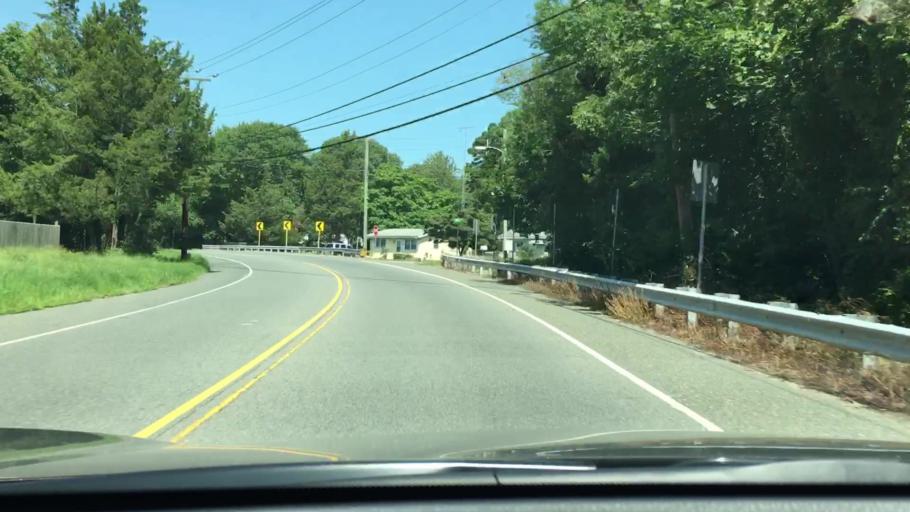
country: US
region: New Jersey
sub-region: Cumberland County
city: Laurel Lake
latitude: 39.3338
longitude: -75.0203
